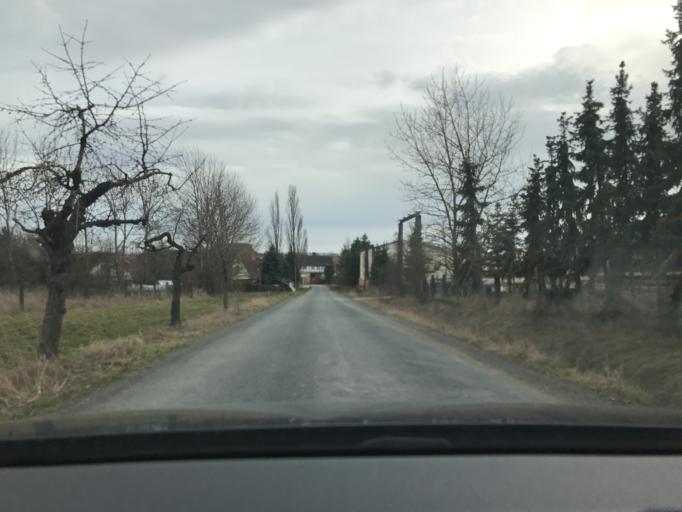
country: DE
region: Thuringia
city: Muehlhausen
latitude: 51.2257
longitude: 10.4198
